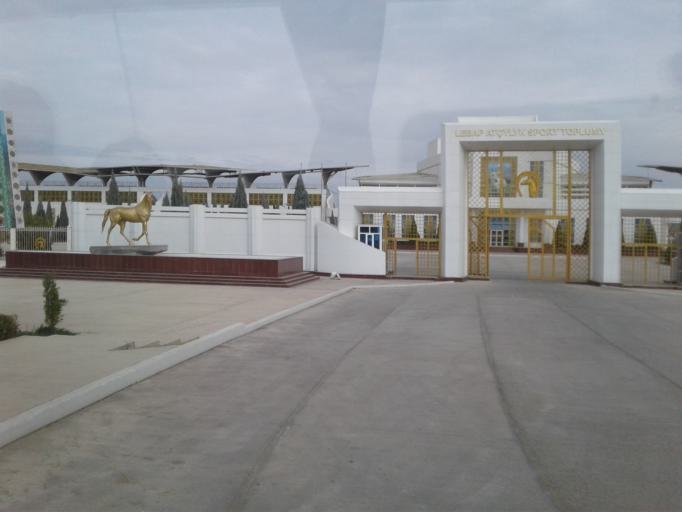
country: TM
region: Lebap
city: Turkmenabat
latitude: 38.9895
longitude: 63.5603
